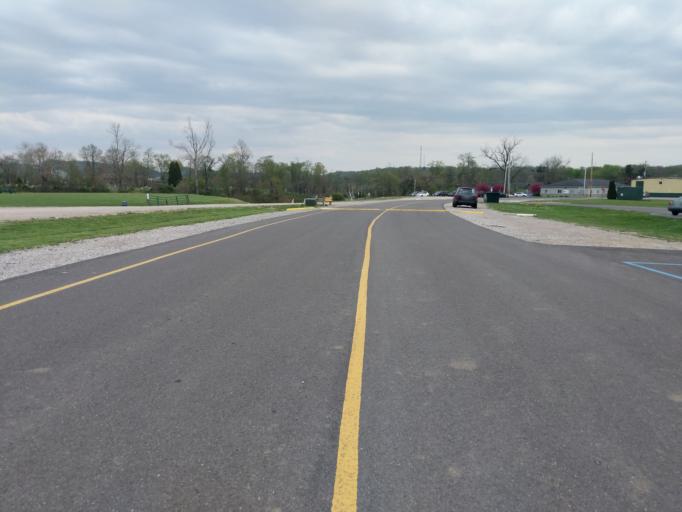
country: US
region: Ohio
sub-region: Athens County
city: The Plains
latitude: 39.3701
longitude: -82.1268
